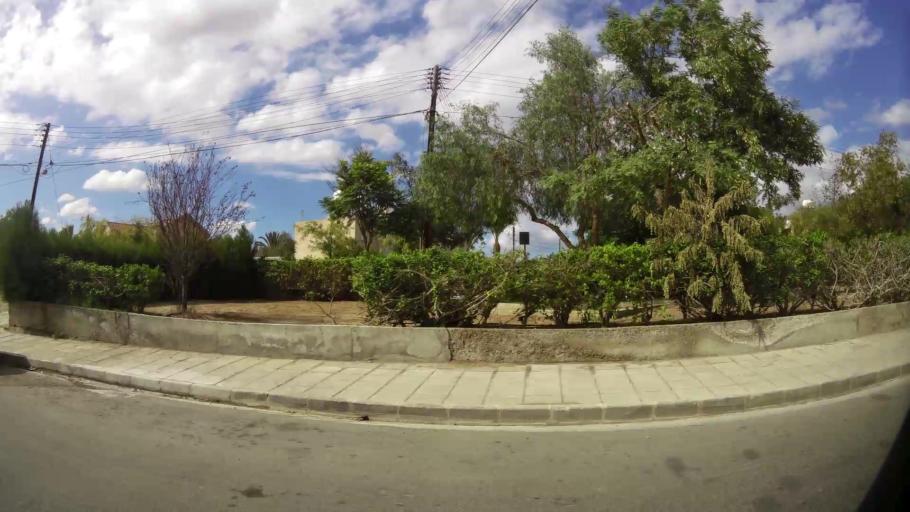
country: CY
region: Lefkosia
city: Nicosia
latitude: 35.1888
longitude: 33.3875
